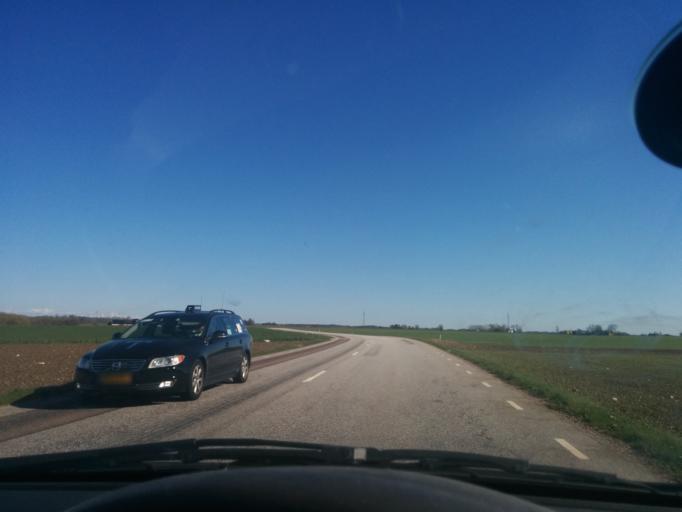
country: SE
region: Skane
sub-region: Svedala Kommun
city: Klagerup
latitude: 55.6301
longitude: 13.2940
